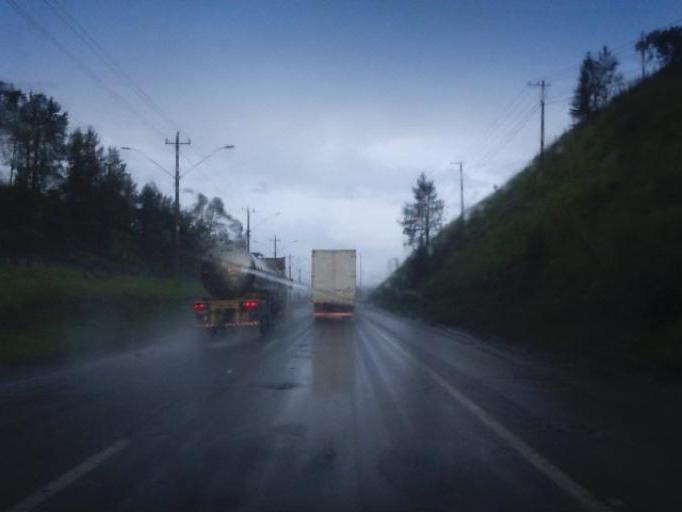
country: BR
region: Sao Paulo
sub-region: Sao Lourenco Da Serra
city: Sao Lourenco da Serra
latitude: -23.8681
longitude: -46.9544
